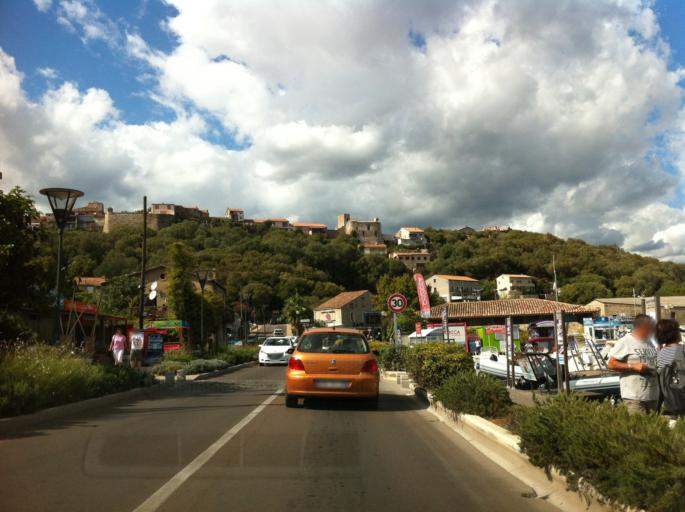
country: FR
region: Corsica
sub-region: Departement de la Corse-du-Sud
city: Porto-Vecchio
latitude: 41.5895
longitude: 9.2835
